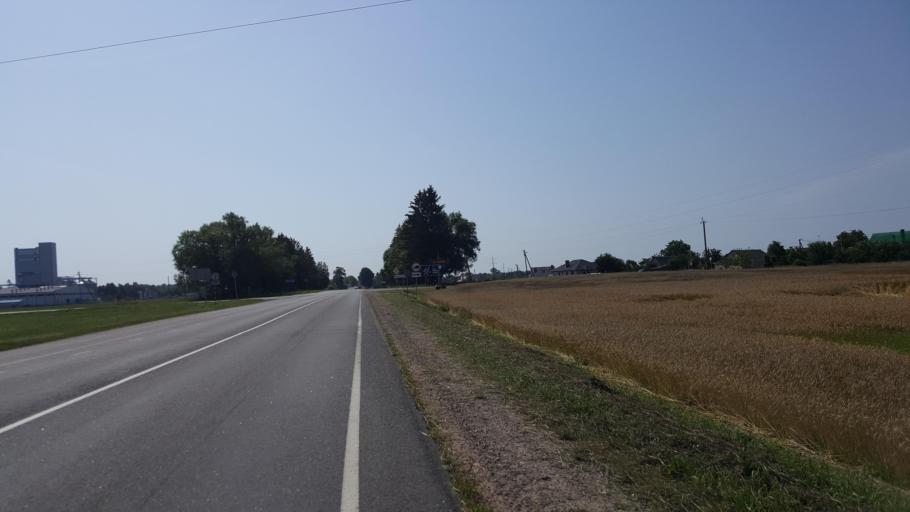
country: BY
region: Brest
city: Zhabinka
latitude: 52.2121
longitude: 23.9994
